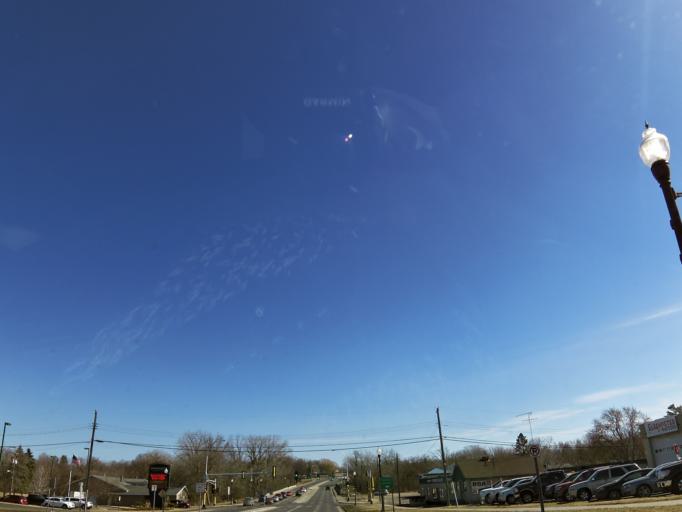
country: US
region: Minnesota
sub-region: Wright County
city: Rockford
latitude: 45.0875
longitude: -93.7373
